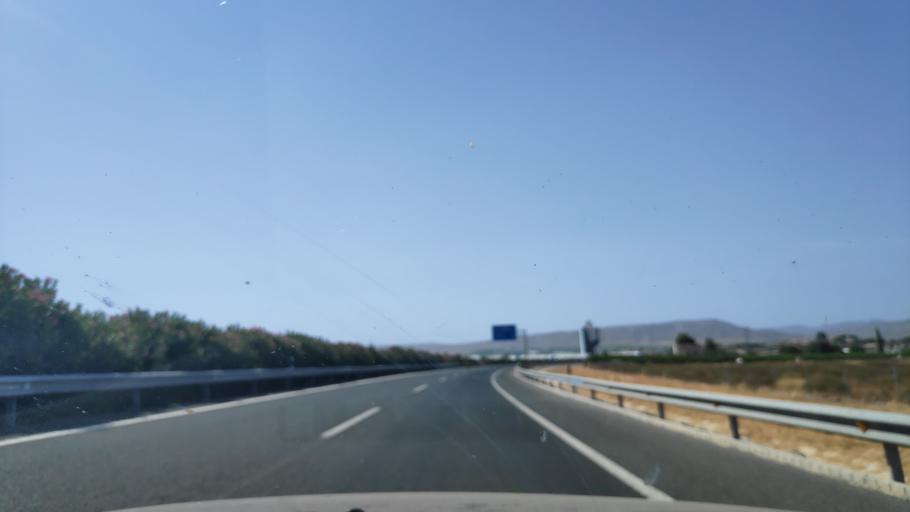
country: ES
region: Murcia
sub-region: Murcia
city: Blanca
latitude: 38.2072
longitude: -1.3495
